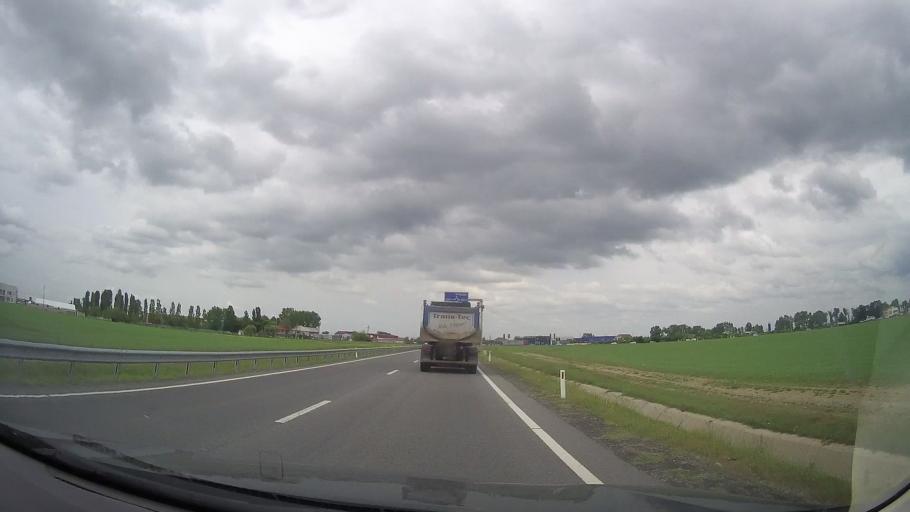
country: RO
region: Dolj
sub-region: Comuna Carcea
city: Carcea
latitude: 44.3112
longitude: 23.9118
